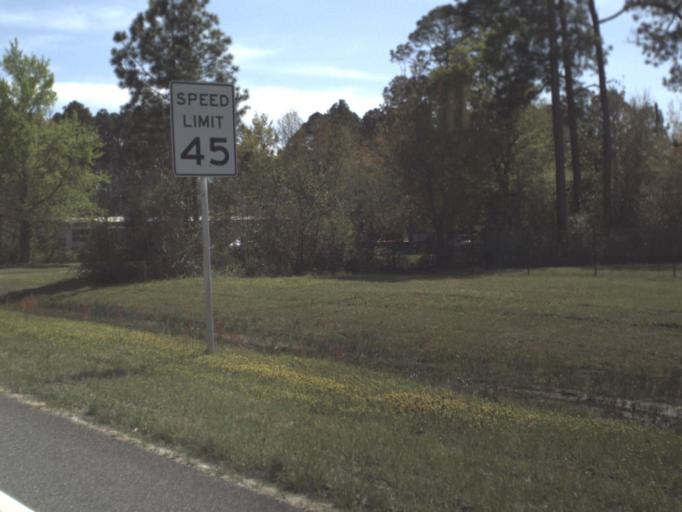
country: US
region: Florida
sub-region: Bay County
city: Lynn Haven
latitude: 30.2957
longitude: -85.6445
